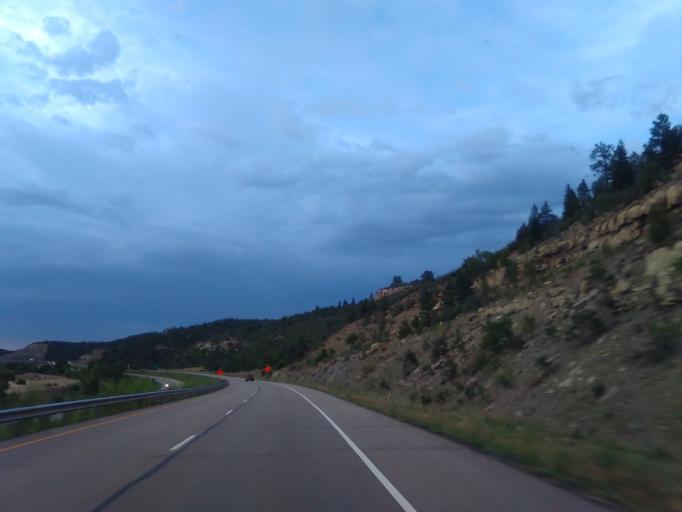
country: US
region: Colorado
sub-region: Las Animas County
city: Trinidad
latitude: 37.0698
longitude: -104.5177
